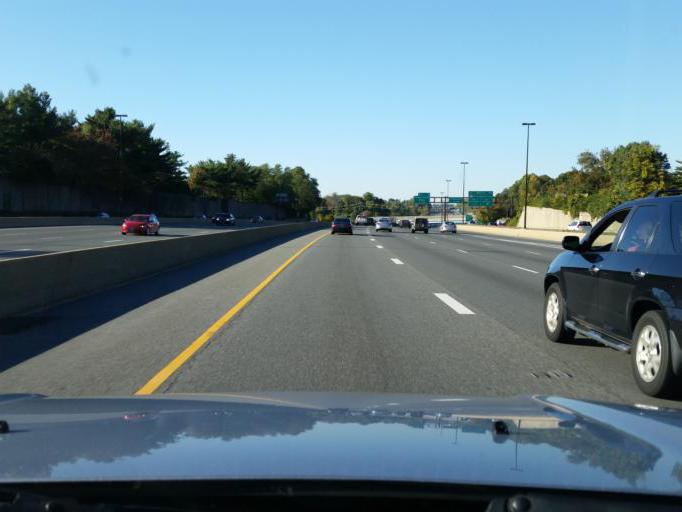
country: US
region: Maryland
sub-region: Montgomery County
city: Rockville
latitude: 39.0815
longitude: -77.1715
